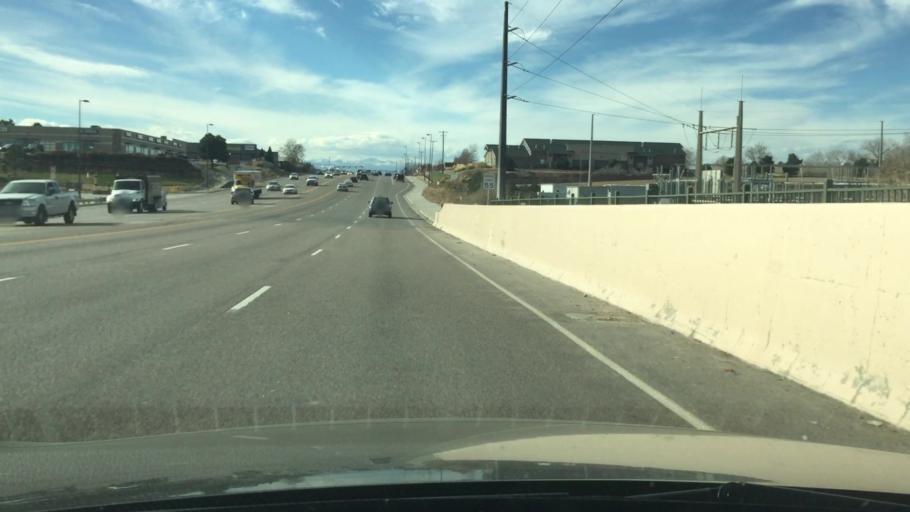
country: US
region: Colorado
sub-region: Arapahoe County
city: Dove Valley
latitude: 39.5951
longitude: -104.8144
